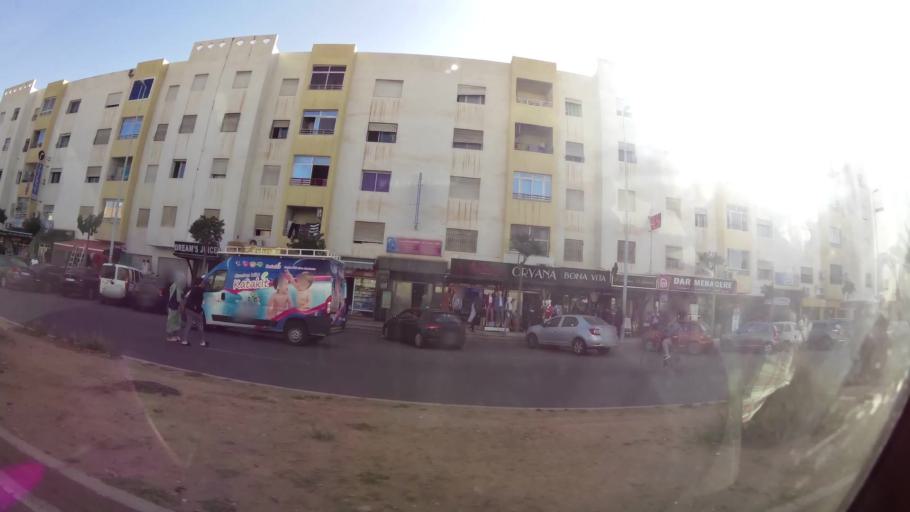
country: MA
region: Oued ed Dahab-Lagouira
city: Dakhla
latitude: 30.3968
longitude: -9.5481
